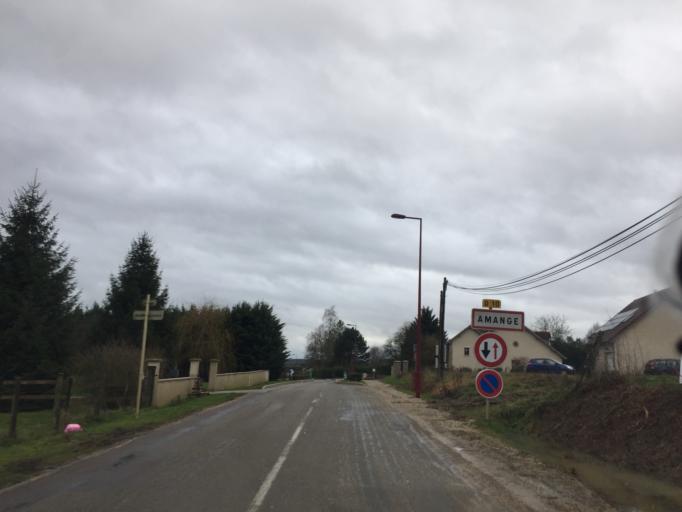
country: FR
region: Franche-Comte
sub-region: Departement du Jura
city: Orchamps
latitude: 47.1688
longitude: 5.5671
